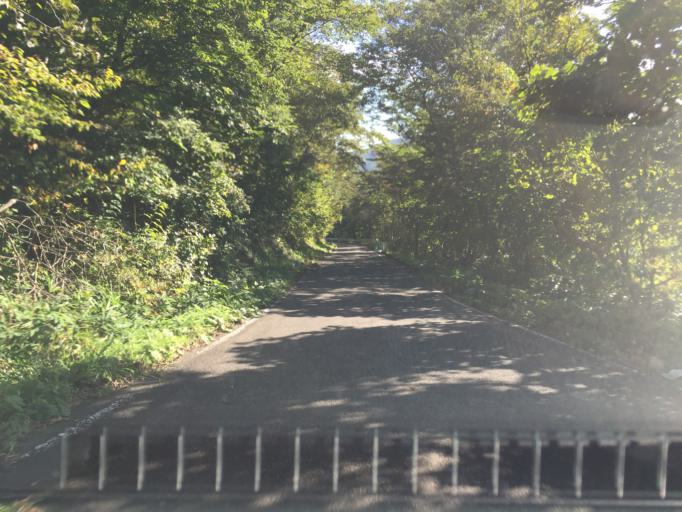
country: JP
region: Fukushima
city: Yanagawamachi-saiwaicho
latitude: 37.8356
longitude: 140.7001
